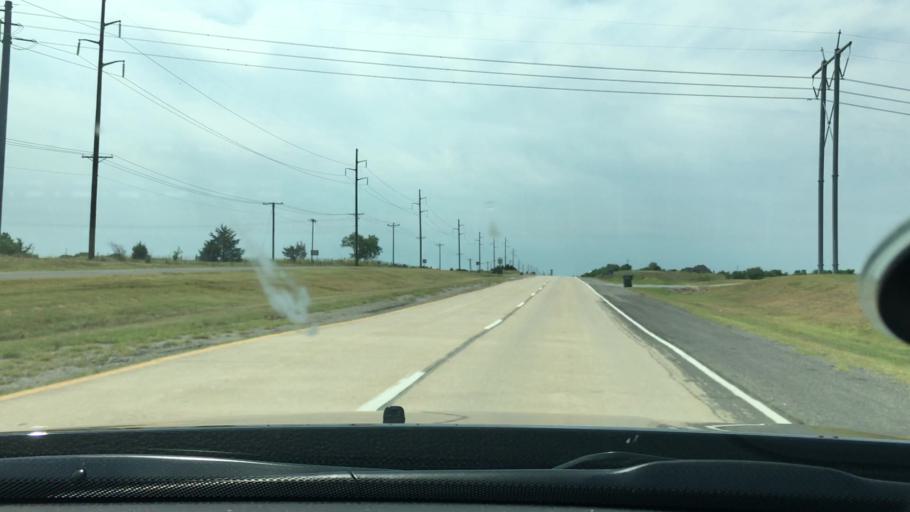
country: US
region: Oklahoma
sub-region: Carter County
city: Ardmore
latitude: 34.2326
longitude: -97.1433
